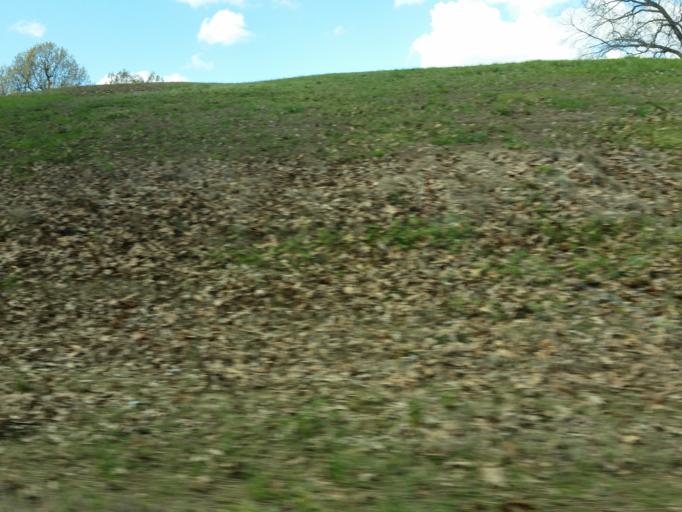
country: US
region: Arkansas
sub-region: Craighead County
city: Bono
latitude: 35.9966
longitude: -90.7091
